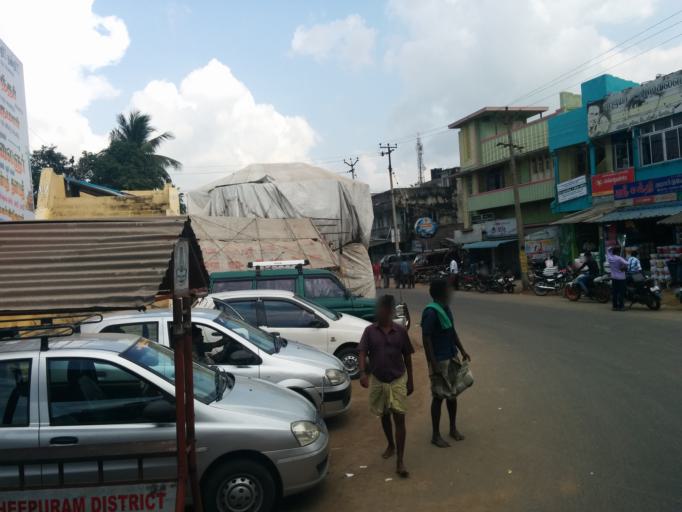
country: IN
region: Tamil Nadu
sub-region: Kancheepuram
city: Madurantakam
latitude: 12.5103
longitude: 79.8851
